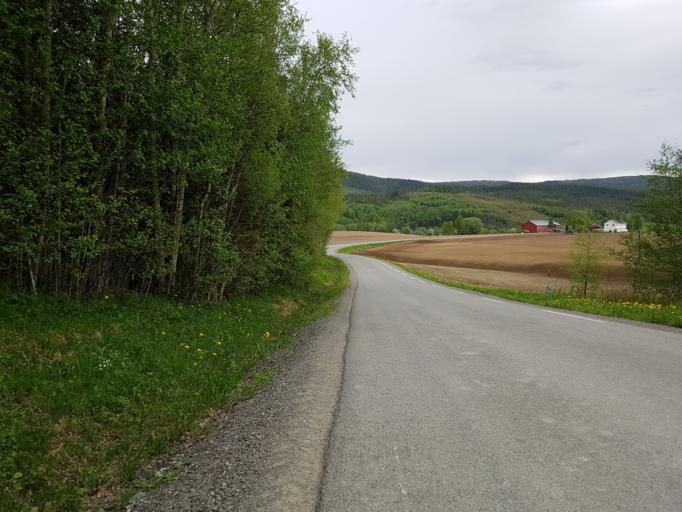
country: NO
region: Nord-Trondelag
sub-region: Levanger
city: Skogn
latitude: 63.6224
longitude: 11.2795
